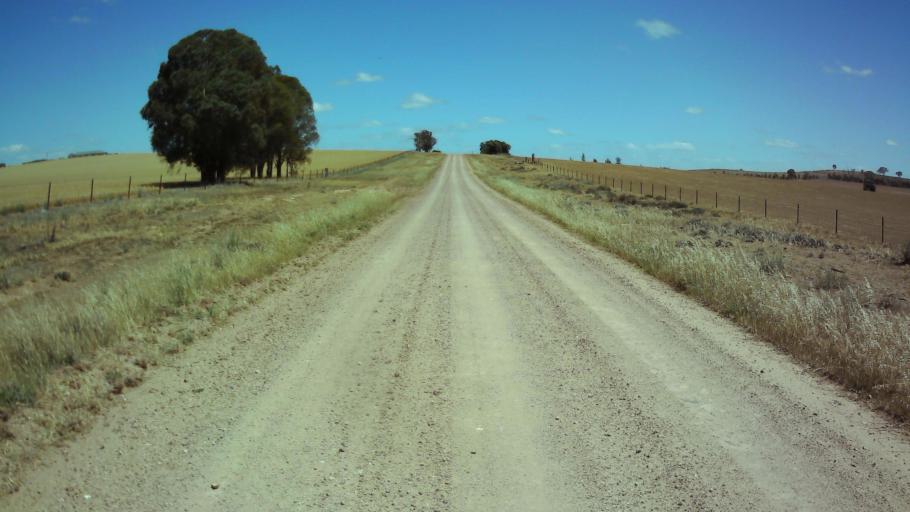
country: AU
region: New South Wales
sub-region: Weddin
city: Grenfell
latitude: -33.9468
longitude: 148.3291
